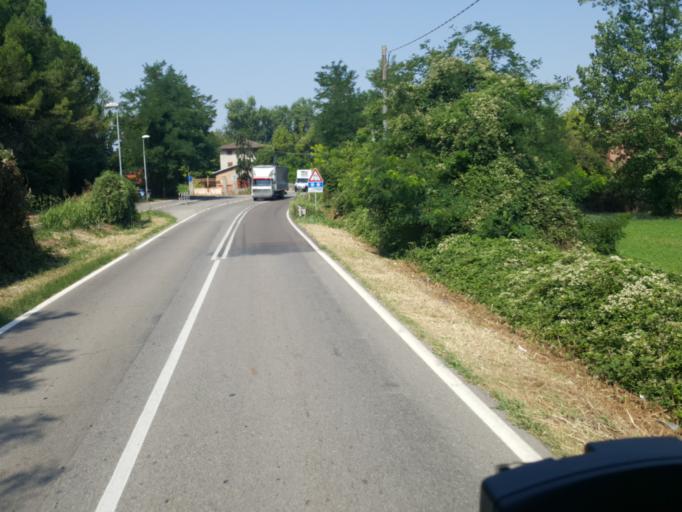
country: IT
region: Emilia-Romagna
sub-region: Provincia di Modena
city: Ca' di Sola
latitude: 44.5399
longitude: 10.9659
